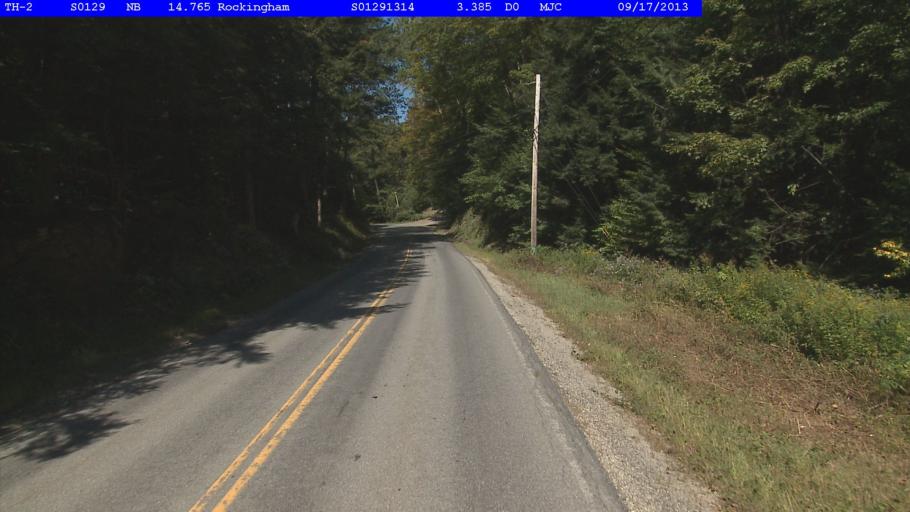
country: US
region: Vermont
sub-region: Windham County
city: Rockingham
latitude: 43.1660
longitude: -72.5172
